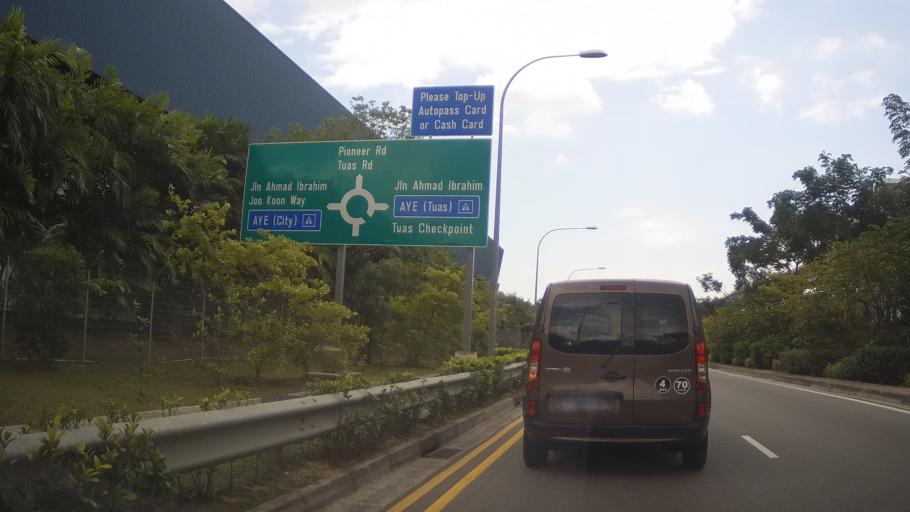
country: MY
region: Johor
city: Johor Bahru
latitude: 1.3248
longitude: 103.6651
